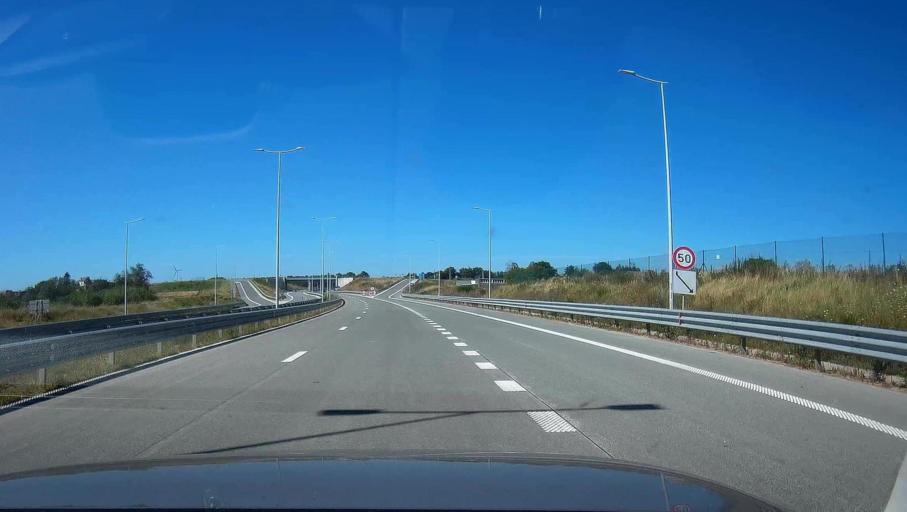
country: BE
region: Wallonia
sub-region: Province de Namur
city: Couvin
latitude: 50.0512
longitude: 4.5114
